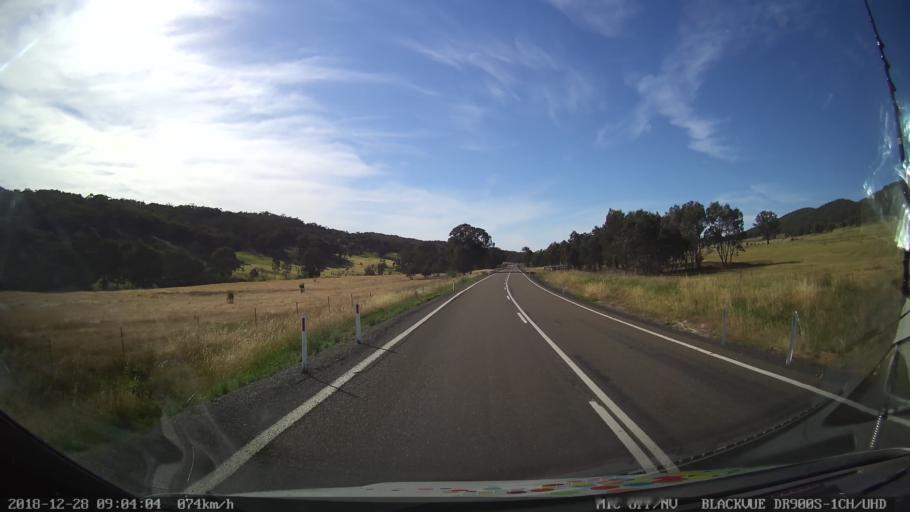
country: AU
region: New South Wales
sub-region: Upper Lachlan Shire
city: Crookwell
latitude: -34.1690
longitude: 149.3415
